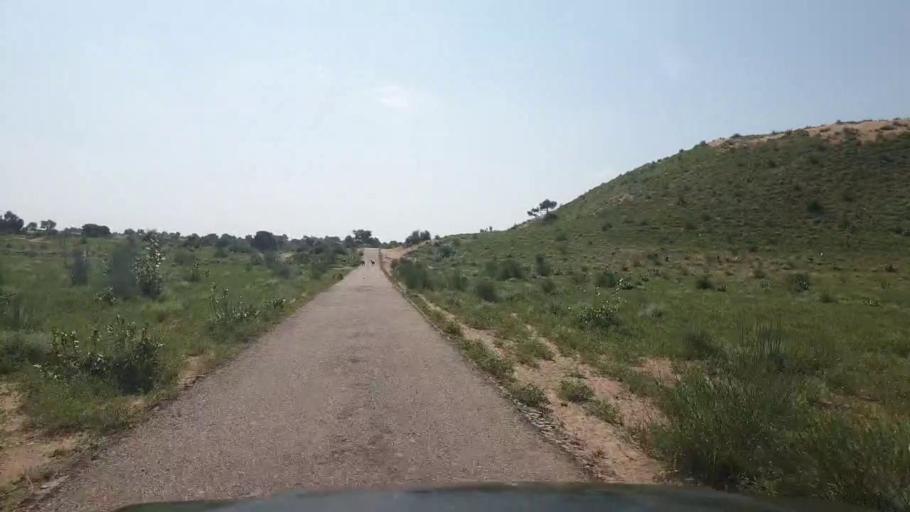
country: PK
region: Sindh
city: Islamkot
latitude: 25.1602
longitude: 70.4079
